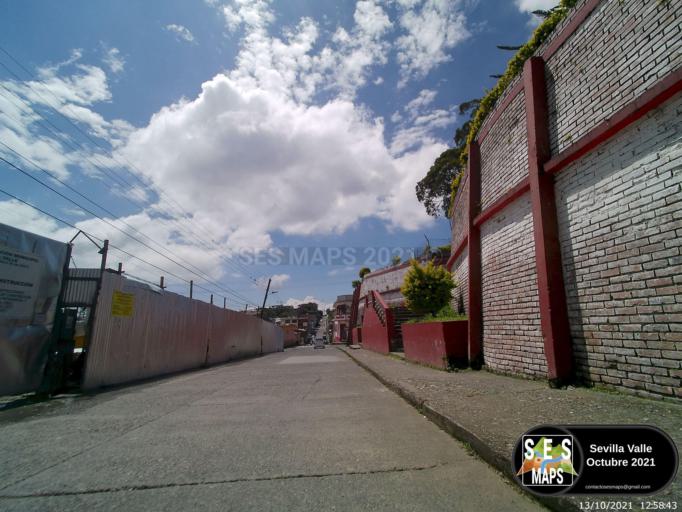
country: CO
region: Valle del Cauca
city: Sevilla
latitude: 4.2689
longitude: -75.9332
